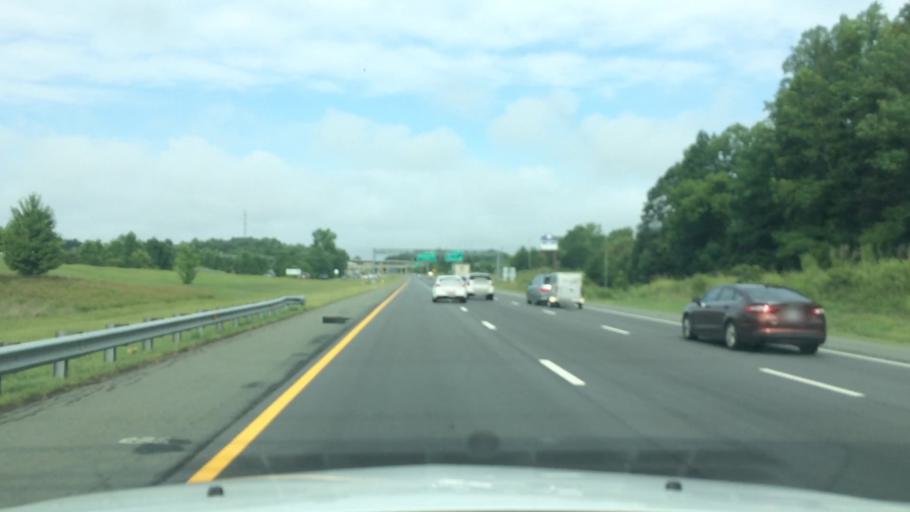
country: US
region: North Carolina
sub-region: Guilford County
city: McLeansville
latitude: 36.0597
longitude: -79.6779
